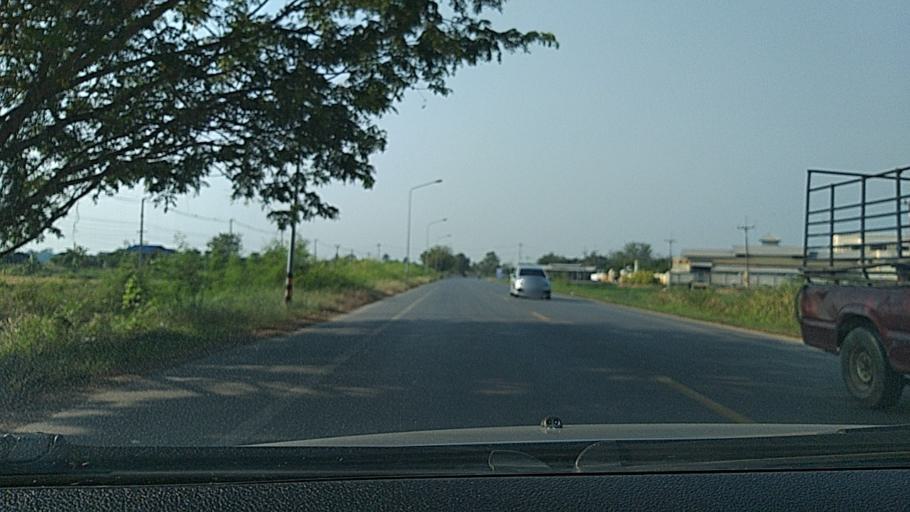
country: TH
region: Sing Buri
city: Phrom Buri
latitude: 14.8181
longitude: 100.4315
